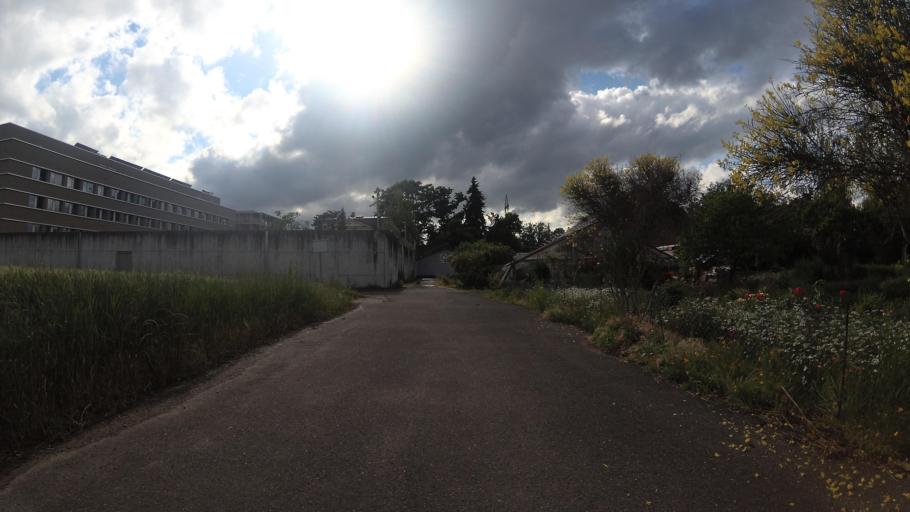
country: DE
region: Baden-Wuerttemberg
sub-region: Freiburg Region
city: Weil am Rhein
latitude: 47.5795
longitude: 7.6056
